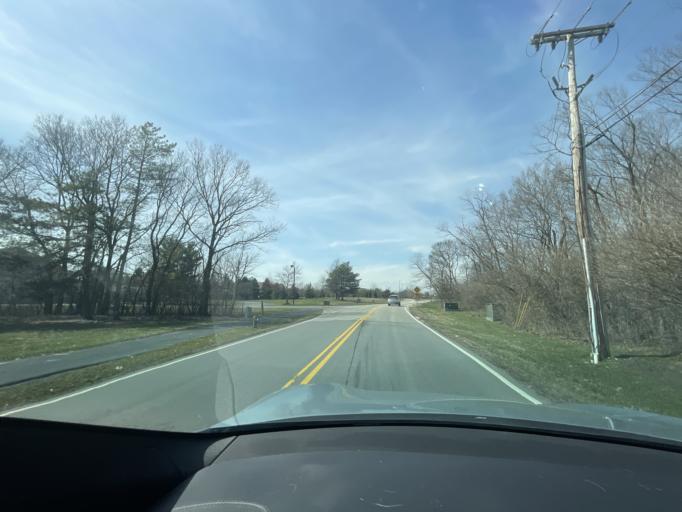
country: US
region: Ohio
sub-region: Franklin County
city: Dublin
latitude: 40.1266
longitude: -83.1467
